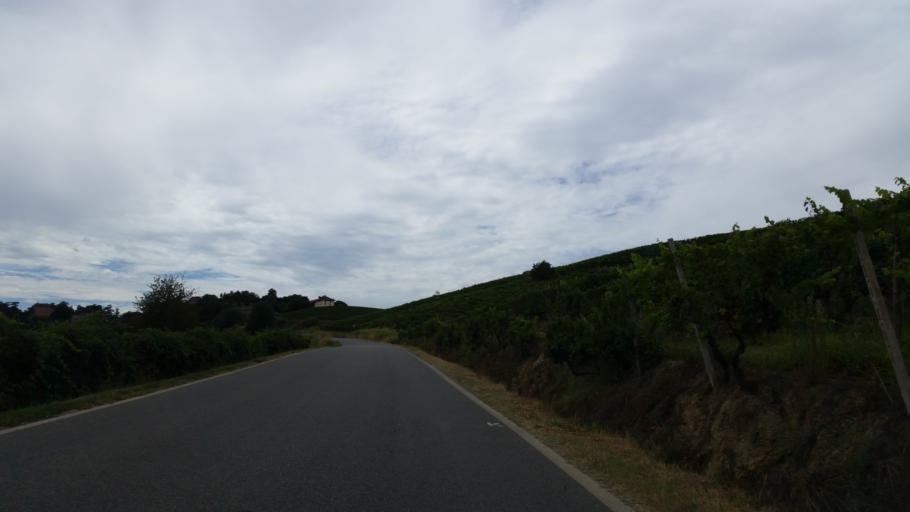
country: IT
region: Piedmont
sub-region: Provincia di Asti
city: San Martino Alfieri
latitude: 44.8220
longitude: 8.1229
